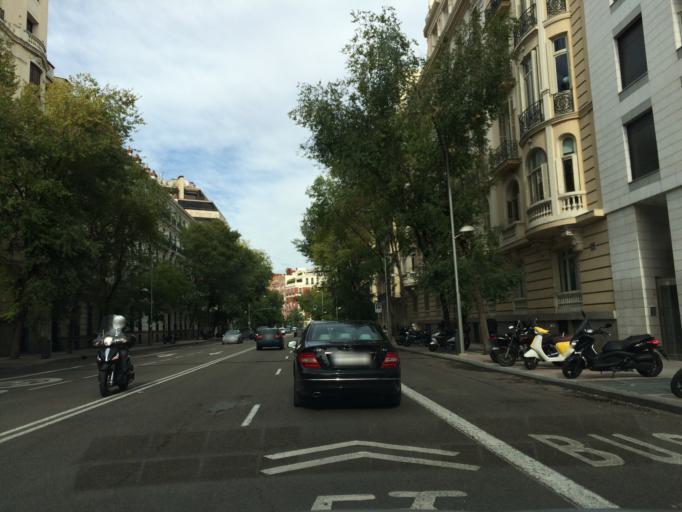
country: ES
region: Madrid
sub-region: Provincia de Madrid
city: Chamberi
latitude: 40.4307
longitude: -3.6925
